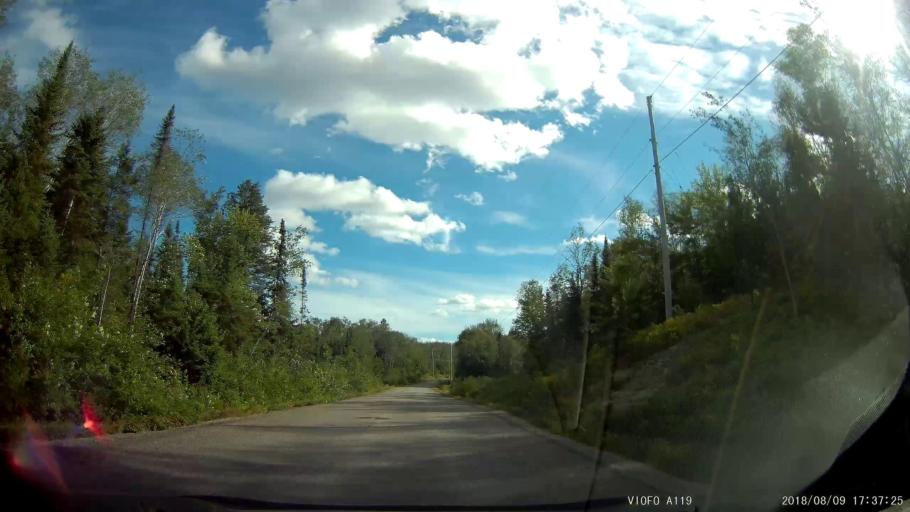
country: CA
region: Ontario
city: Rayside-Balfour
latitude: 46.6092
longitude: -81.4742
